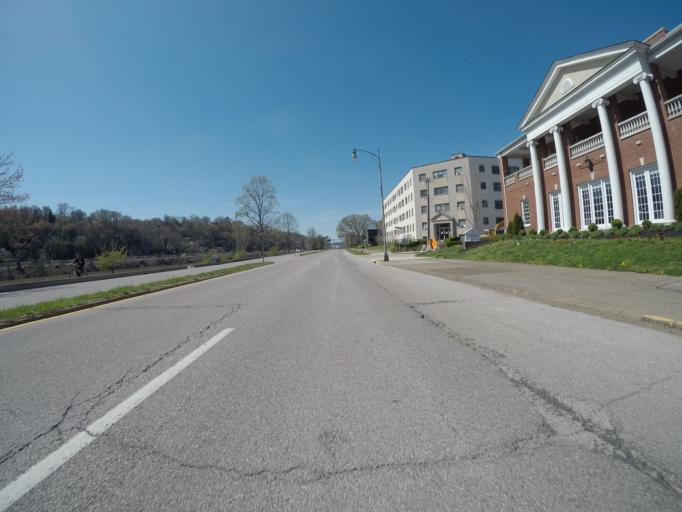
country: US
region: West Virginia
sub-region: Kanawha County
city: Charleston
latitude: 38.3416
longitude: -81.6283
